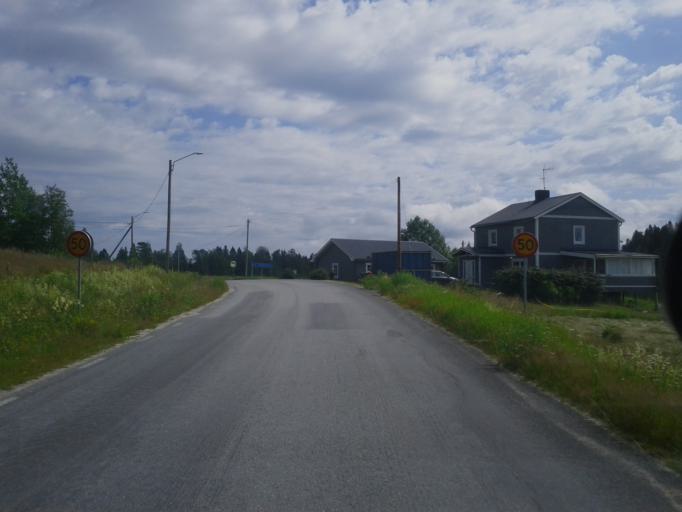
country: SE
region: Vaesternorrland
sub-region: OErnskoeldsviks Kommun
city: Ornskoldsvik
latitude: 63.2876
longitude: 18.8406
